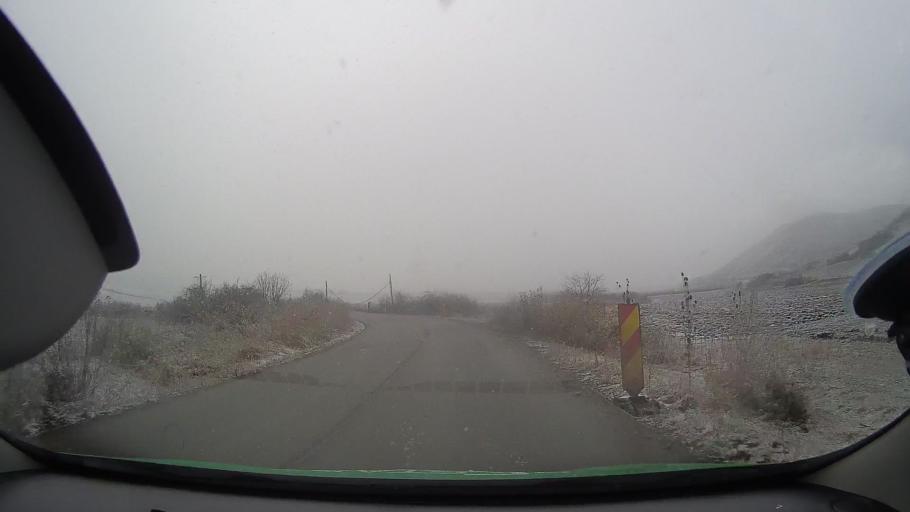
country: RO
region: Alba
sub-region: Comuna Noslac
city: Noslac
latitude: 46.3748
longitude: 23.9162
